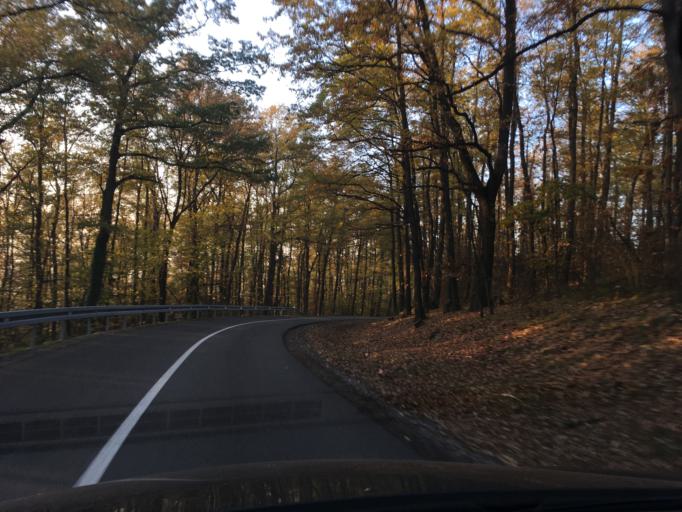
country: RS
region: Central Serbia
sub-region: Belgrade
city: Sopot
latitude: 44.4729
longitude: 20.5743
